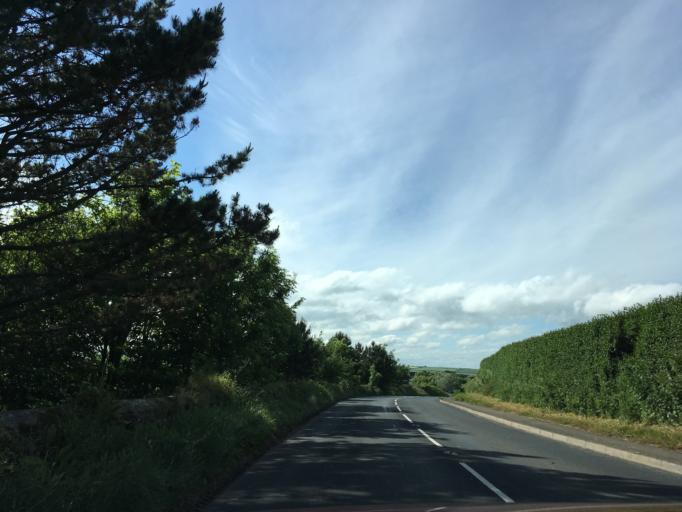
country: GB
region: England
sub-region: Devon
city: Dartmouth
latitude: 50.3448
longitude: -3.5923
